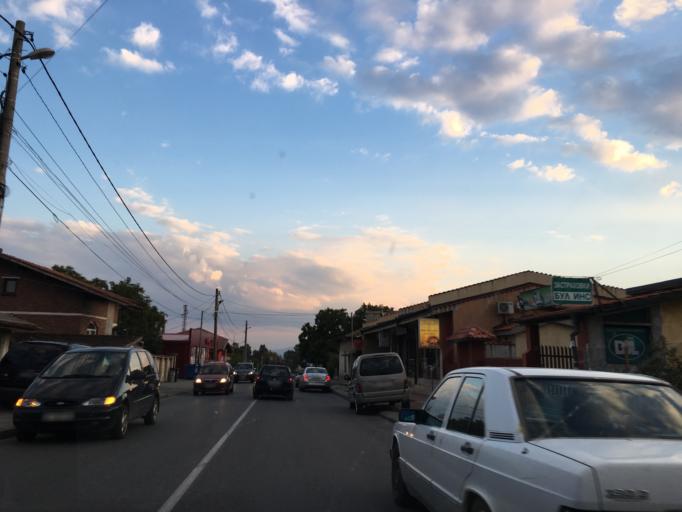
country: BG
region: Sofia-Capital
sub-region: Stolichna Obshtina
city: Sofia
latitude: 42.8241
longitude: 23.3540
